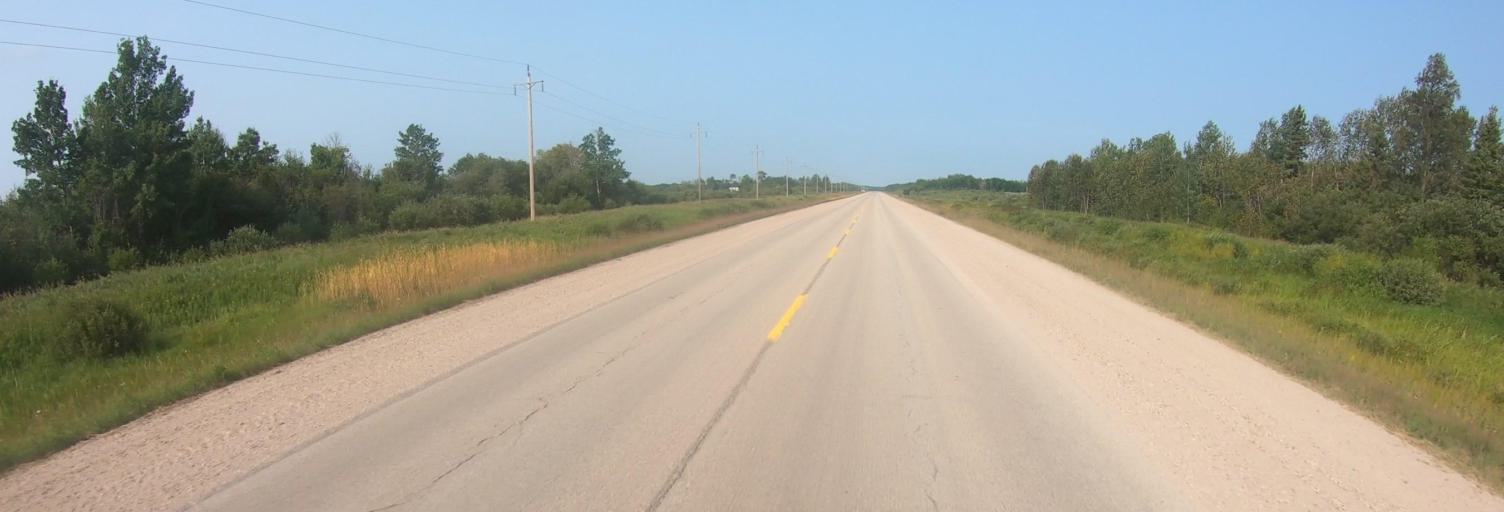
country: US
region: Minnesota
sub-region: Roseau County
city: Roseau
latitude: 49.0236
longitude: -95.6899
